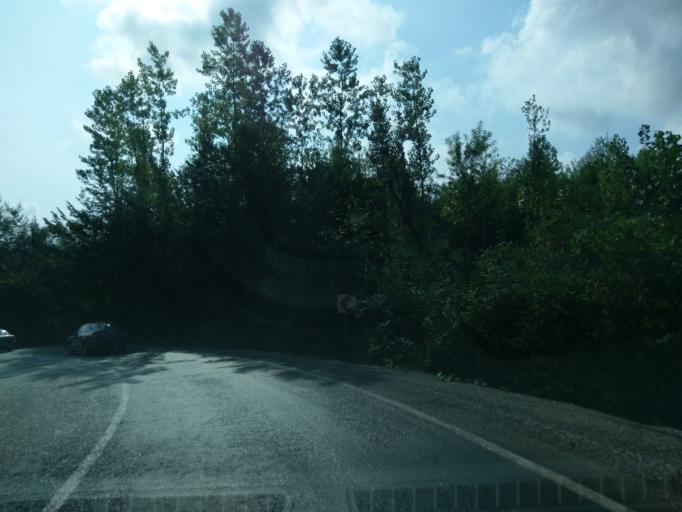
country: TR
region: Sinop
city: Ayancik
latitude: 41.8789
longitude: 34.5192
